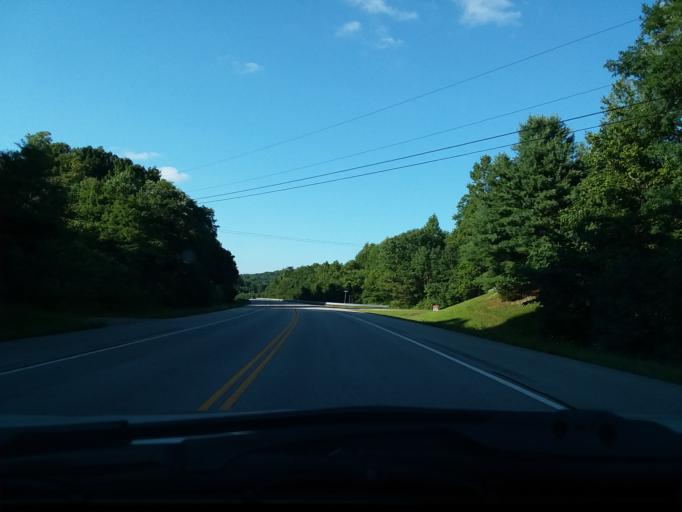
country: US
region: Tennessee
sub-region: Clay County
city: Celina
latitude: 36.5808
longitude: -85.4436
